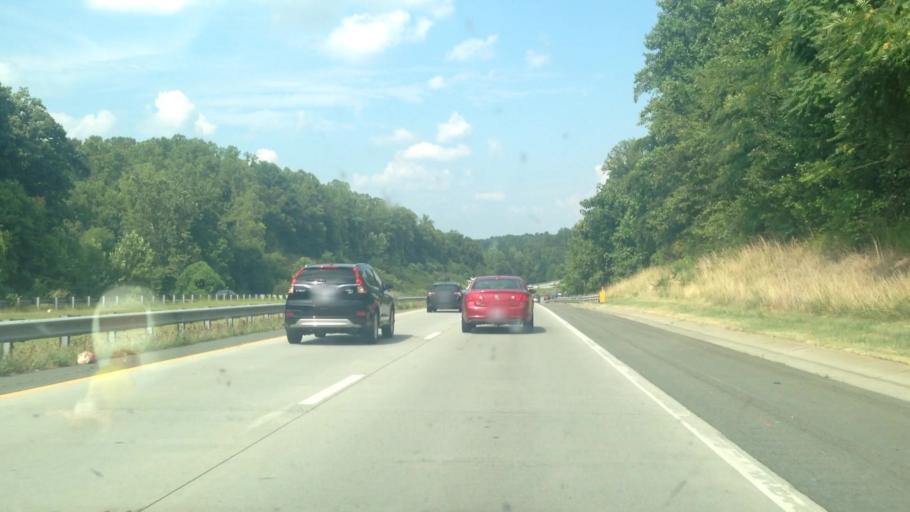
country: US
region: North Carolina
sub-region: Forsyth County
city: Winston-Salem
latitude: 36.1029
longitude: -80.1910
